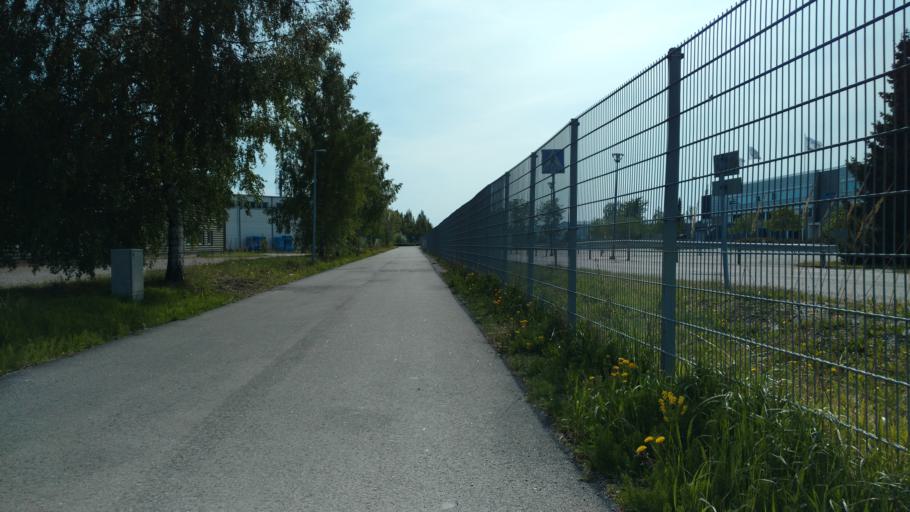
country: FI
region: Varsinais-Suomi
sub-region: Salo
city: Salo
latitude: 60.3894
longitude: 23.1096
